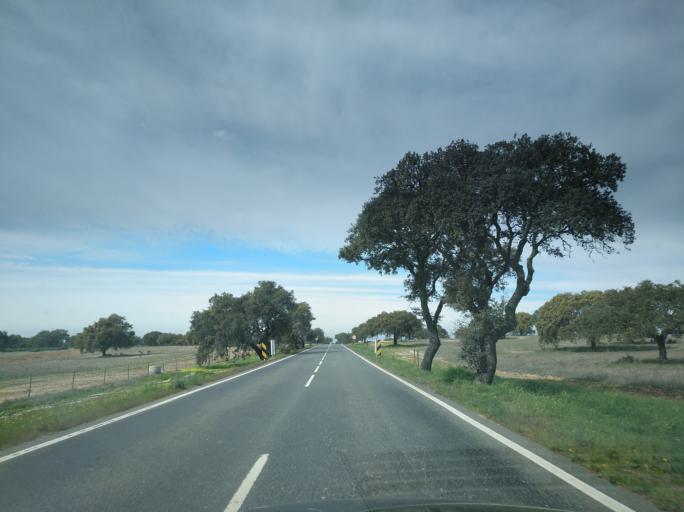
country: PT
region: Beja
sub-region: Mertola
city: Mertola
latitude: 37.7552
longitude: -7.8087
